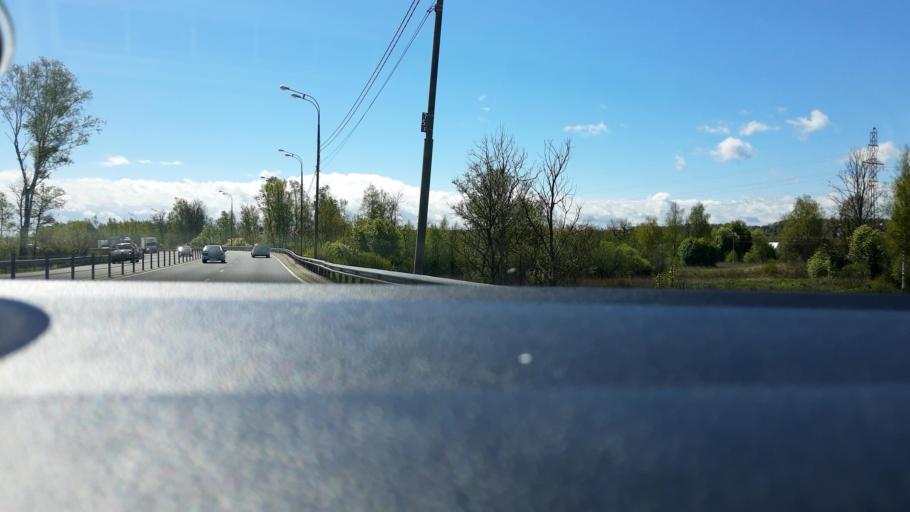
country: RU
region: Moskovskaya
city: Dedenevo
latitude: 56.2709
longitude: 37.5024
